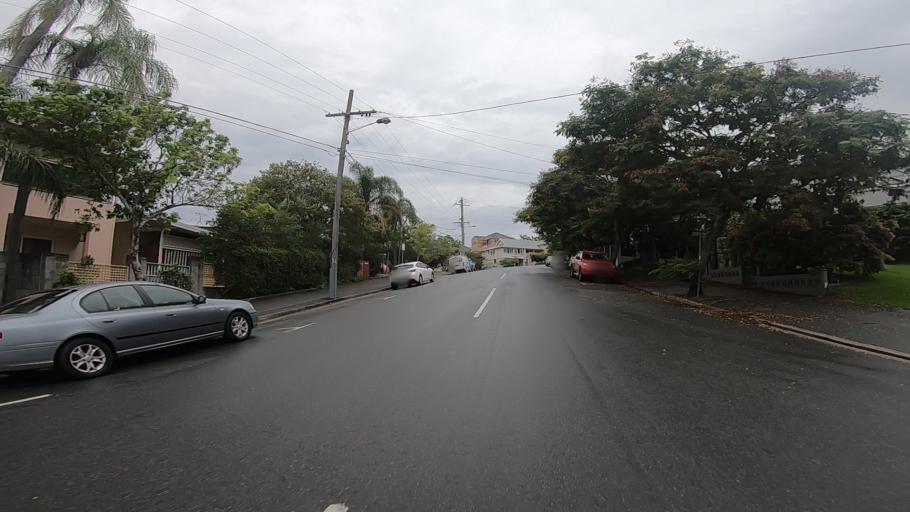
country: AU
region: Queensland
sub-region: Brisbane
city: Fortitude Valley
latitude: -27.4473
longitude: 153.0389
